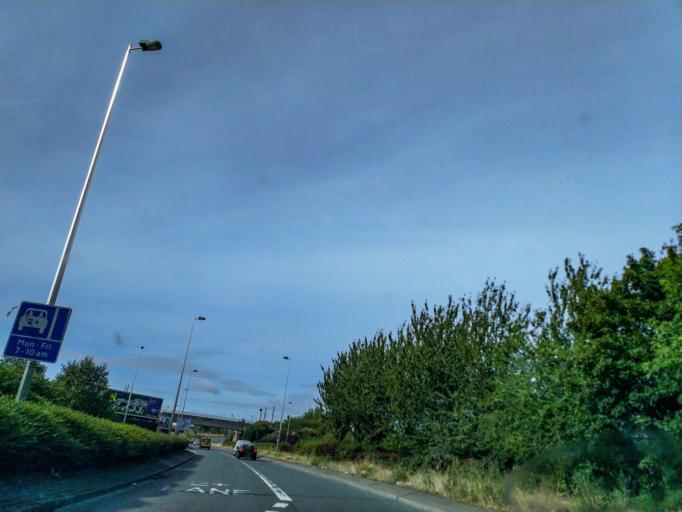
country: GB
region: England
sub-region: City and Borough of Birmingham
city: Birmingham
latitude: 52.5009
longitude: -1.8576
